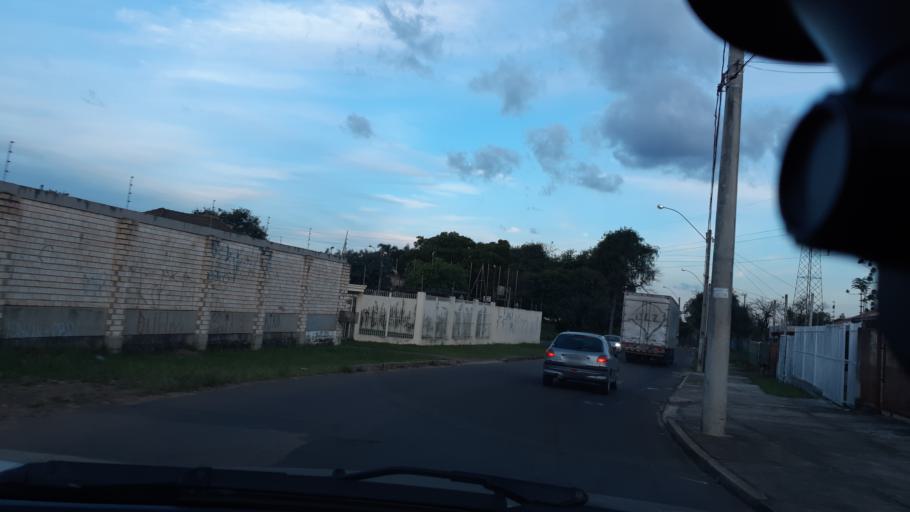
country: BR
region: Rio Grande do Sul
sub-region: Sapucaia Do Sul
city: Sapucaia
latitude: -29.8449
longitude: -51.1478
